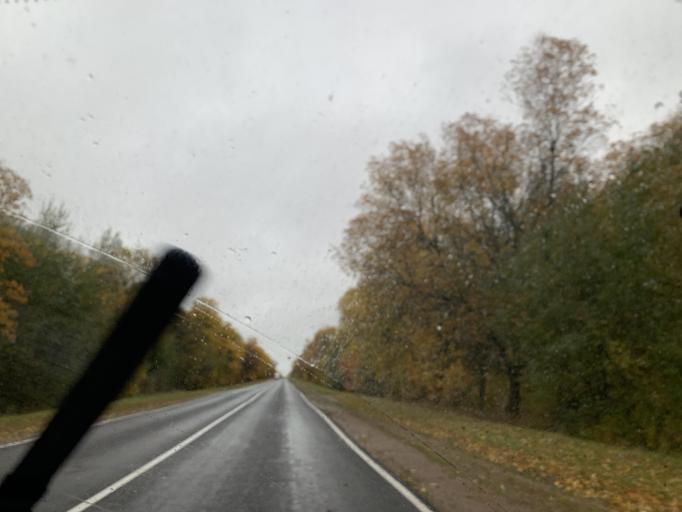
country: BY
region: Minsk
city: Novy Svyerzhan'
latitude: 53.4356
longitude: 26.6500
